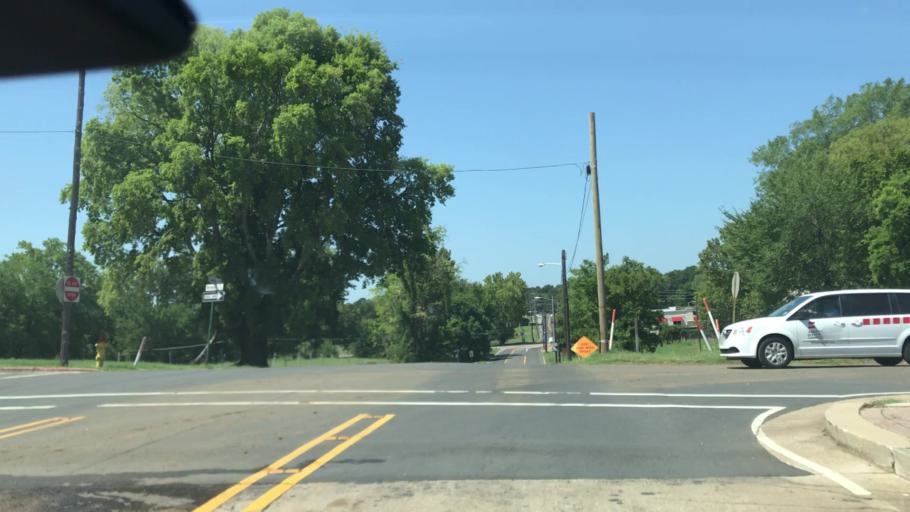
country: US
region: Louisiana
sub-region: Caddo Parish
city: Shreveport
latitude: 32.5147
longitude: -93.7530
